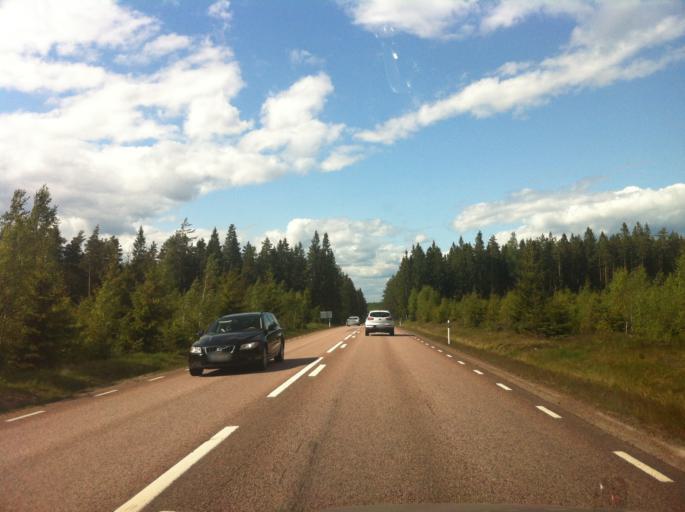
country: SE
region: Vaermland
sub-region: Kristinehamns Kommun
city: Bjorneborg
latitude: 59.2538
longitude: 14.1756
